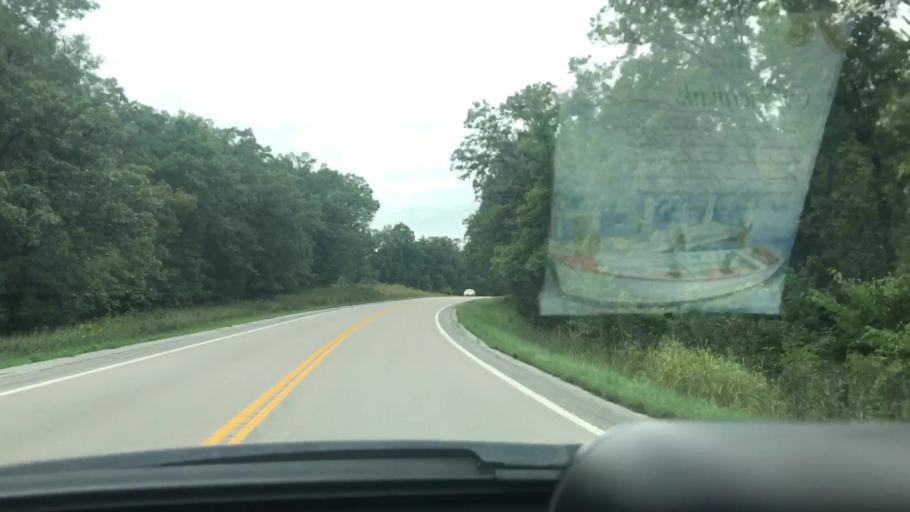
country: US
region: Missouri
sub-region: Benton County
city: Warsaw
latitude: 38.1627
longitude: -93.3032
